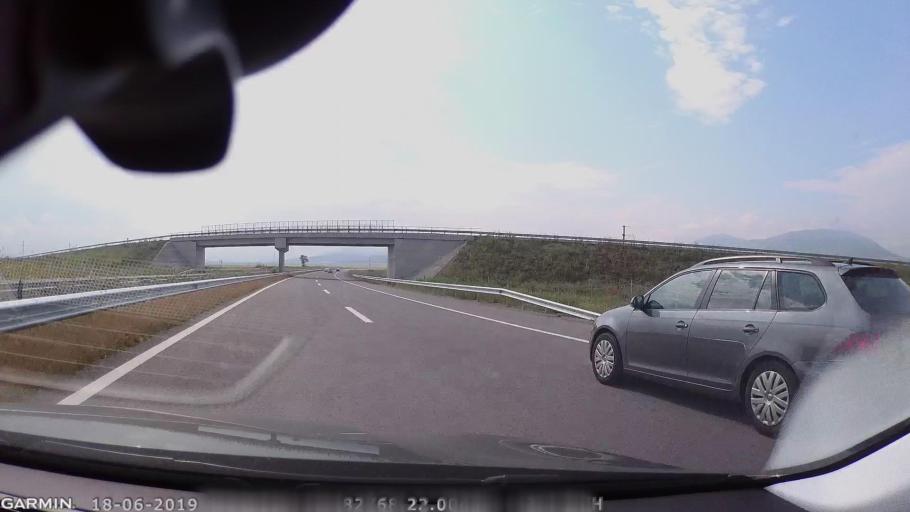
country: MK
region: Sveti Nikole
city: Sveti Nikole
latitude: 41.8403
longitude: 21.9820
